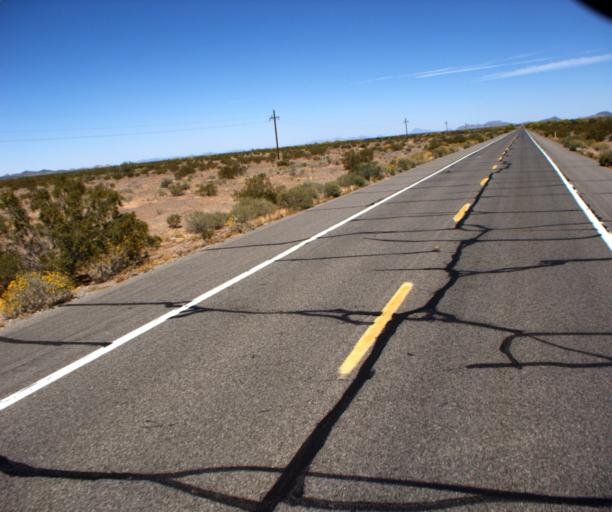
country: US
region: Arizona
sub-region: Pima County
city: Ajo
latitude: 32.5740
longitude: -112.8750
